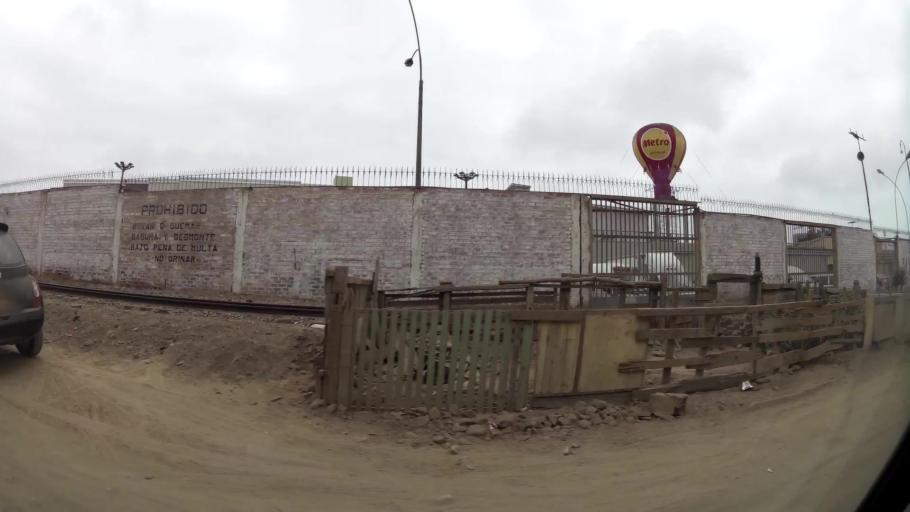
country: PE
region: Callao
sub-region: Callao
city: Callao
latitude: -12.0466
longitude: -77.1116
